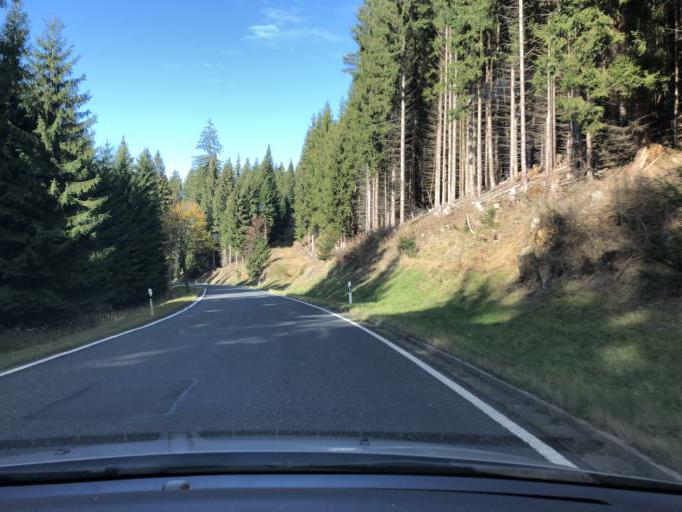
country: DE
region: Thuringia
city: Neuhaus am Rennweg
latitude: 50.5345
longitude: 11.1183
